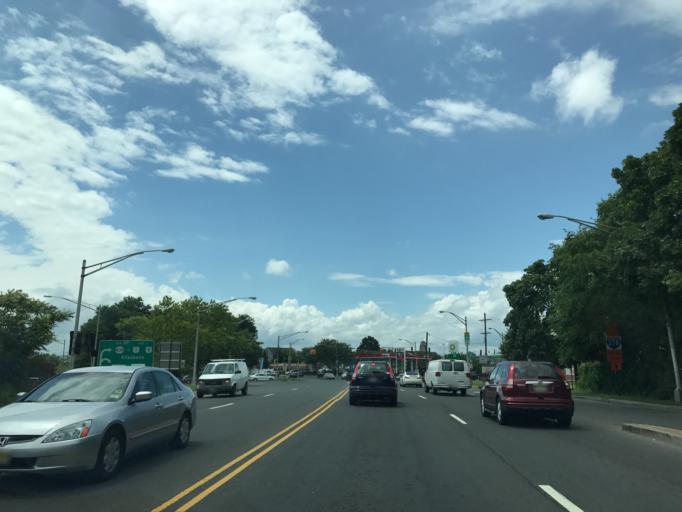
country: US
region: New Jersey
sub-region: Union County
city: Elizabeth
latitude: 40.6441
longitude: -74.2103
